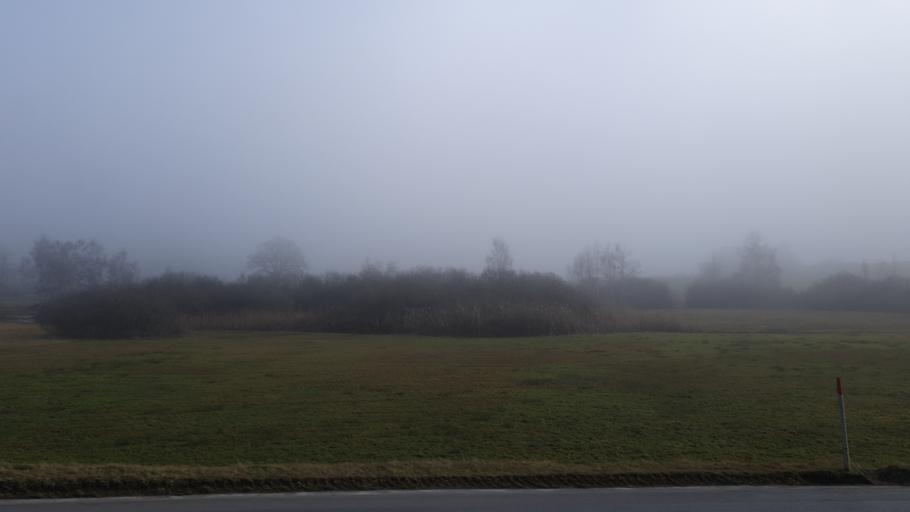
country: CH
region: Fribourg
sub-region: Veveyse District
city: Chatel-Saint-Denis
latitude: 46.5409
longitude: 6.8978
